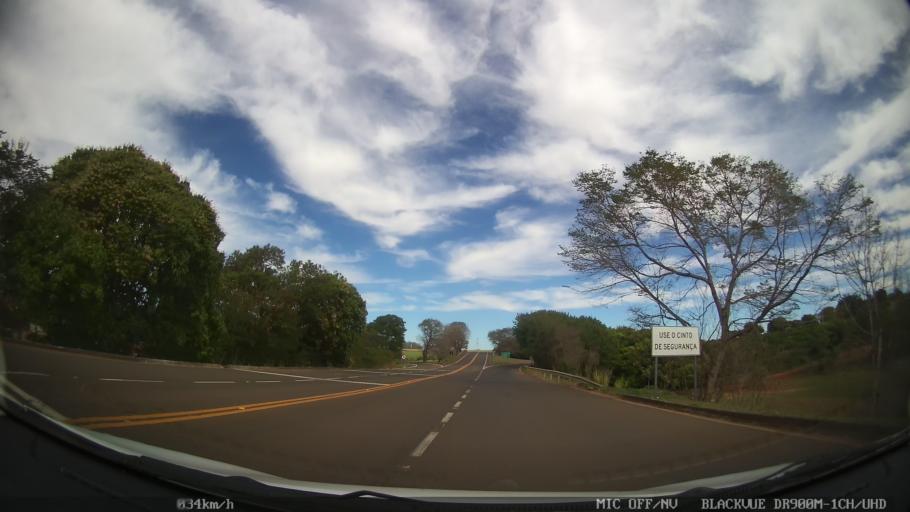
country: BR
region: Sao Paulo
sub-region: Santa Adelia
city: Santa Adelia
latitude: -21.3697
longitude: -48.7480
